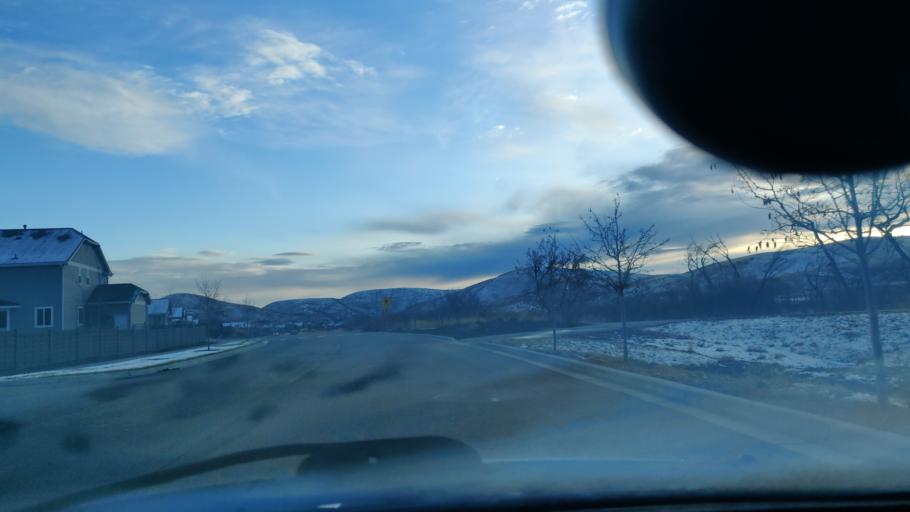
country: US
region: Idaho
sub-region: Ada County
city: Eagle
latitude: 43.7814
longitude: -116.2624
